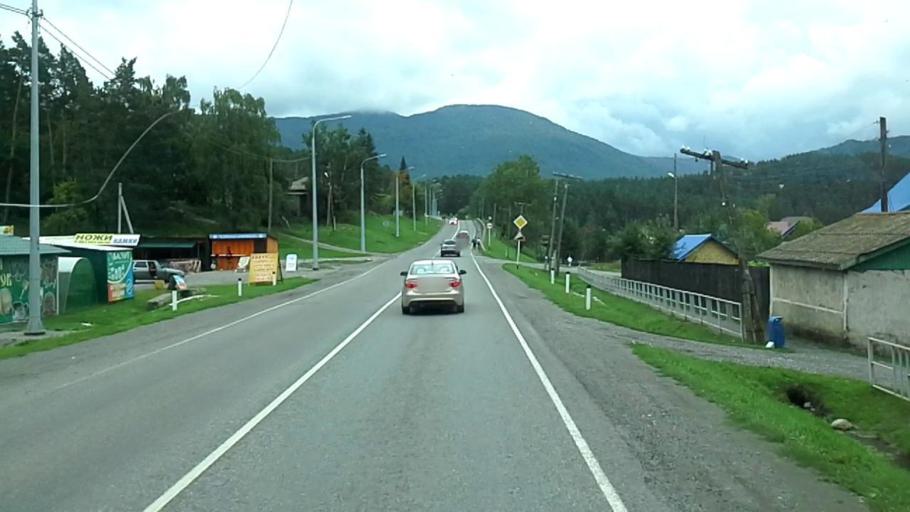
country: RU
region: Altay
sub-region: Mayminskiy Rayon
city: Manzherok
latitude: 51.8323
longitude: 85.7819
